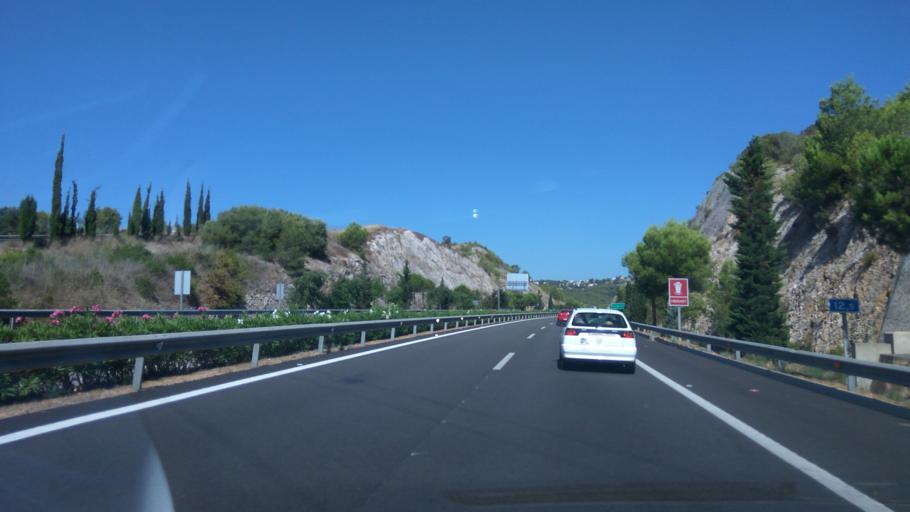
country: ES
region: Catalonia
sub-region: Provincia de Tarragona
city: Cunit
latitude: 41.2100
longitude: 1.6427
